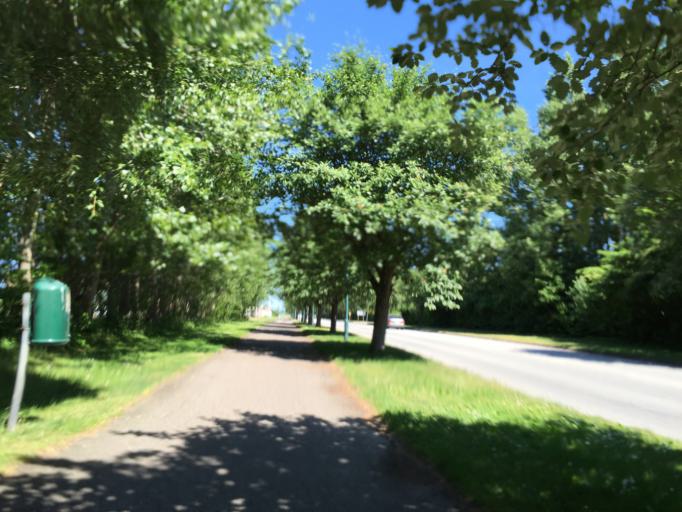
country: SE
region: Skane
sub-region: Trelleborgs Kommun
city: Trelleborg
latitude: 55.3781
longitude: 13.1234
